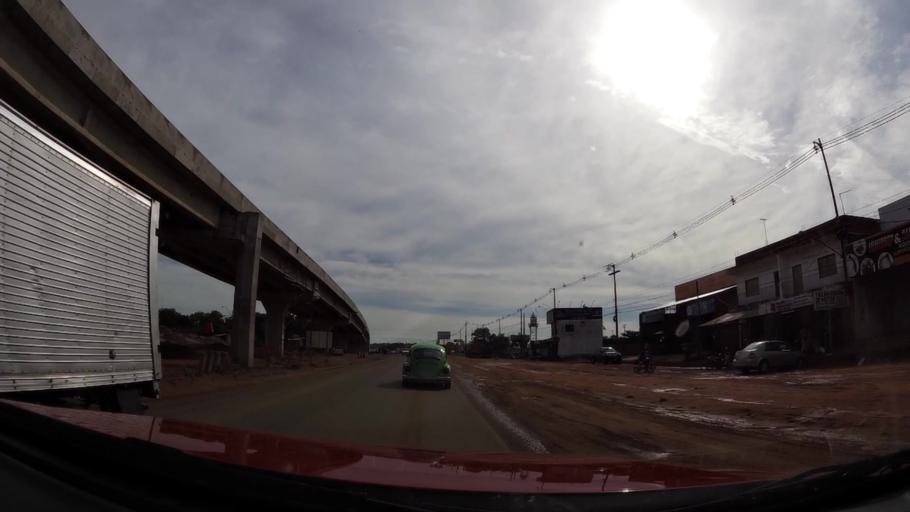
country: PY
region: Central
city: Limpio
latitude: -25.1774
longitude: -57.4864
